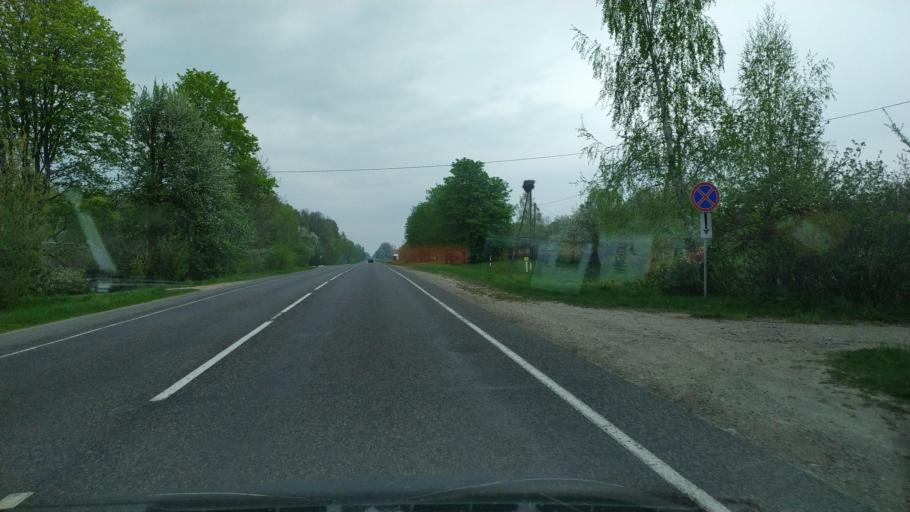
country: BY
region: Brest
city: Horad Kobryn
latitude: 52.2859
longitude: 24.4911
